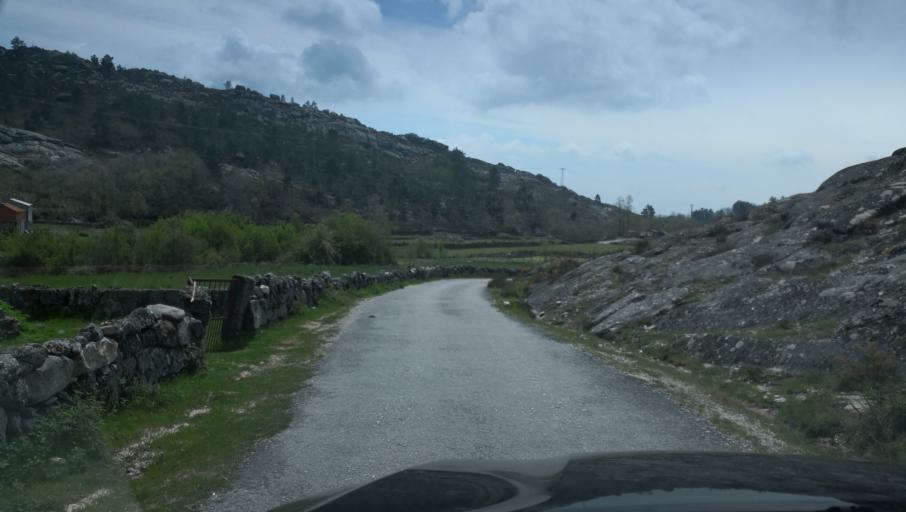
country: PT
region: Vila Real
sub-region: Vila Real
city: Vila Real
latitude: 41.3327
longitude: -7.8005
